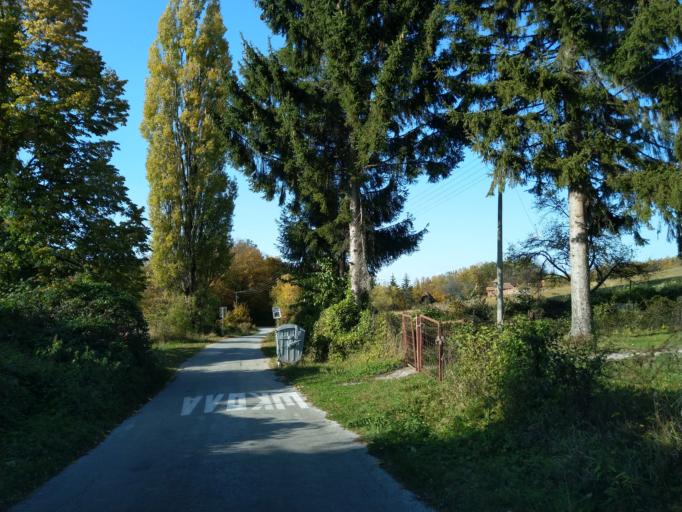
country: RS
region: Central Serbia
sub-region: Zlatiborski Okrug
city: Uzice
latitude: 43.8708
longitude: 19.7549
